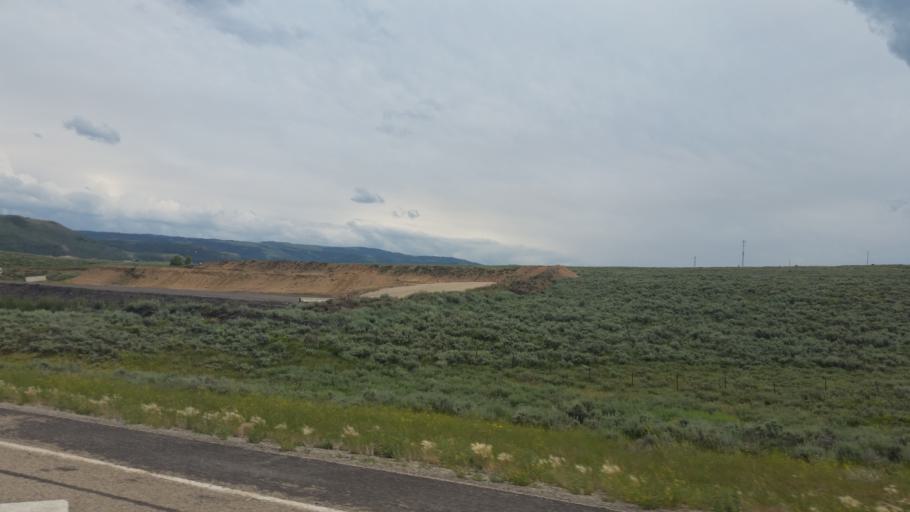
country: US
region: Utah
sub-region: Wasatch County
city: Heber
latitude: 40.1835
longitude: -111.0539
